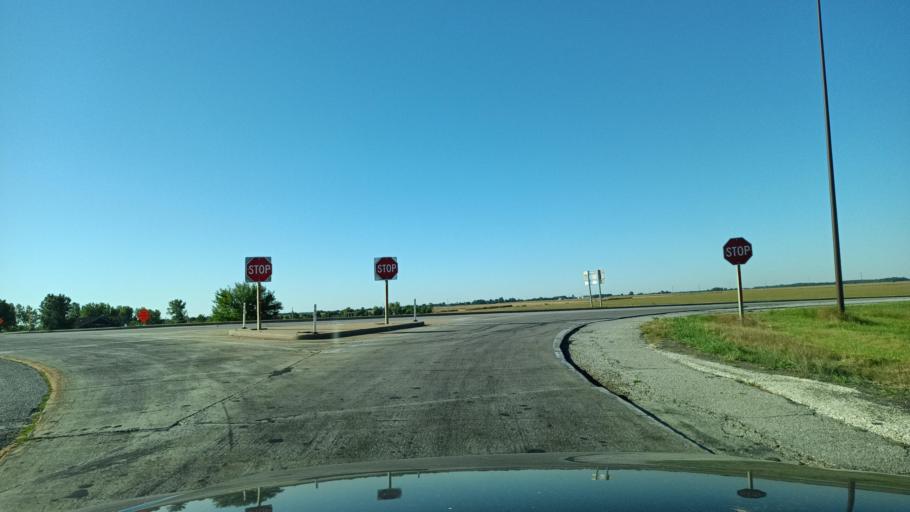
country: US
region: Illinois
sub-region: Warren County
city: Monmouth
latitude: 40.8907
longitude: -90.6636
